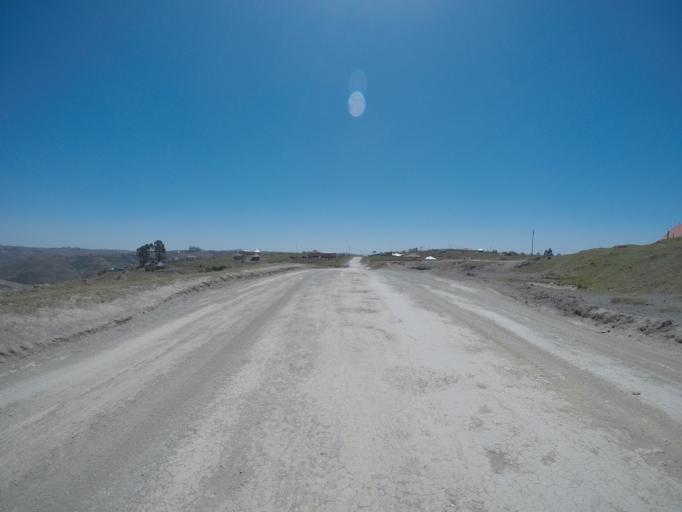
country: ZA
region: Eastern Cape
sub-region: OR Tambo District Municipality
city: Libode
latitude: -31.9433
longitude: 29.0274
